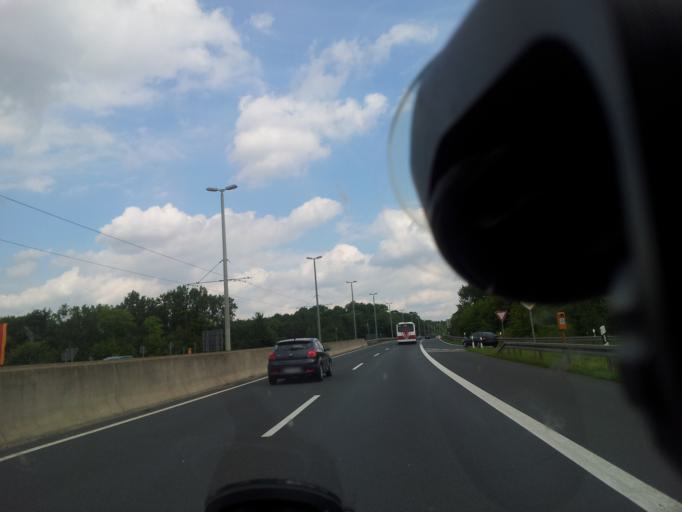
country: DE
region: Lower Saxony
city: Braunschweig
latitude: 52.2356
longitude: 10.5285
